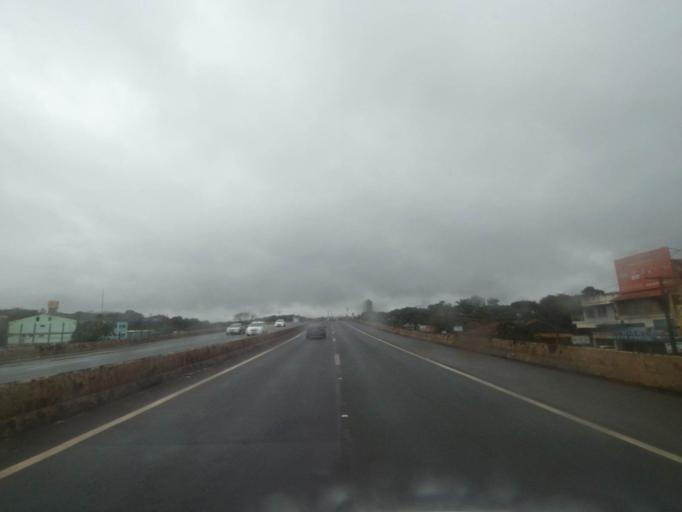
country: PY
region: Alto Parana
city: Ciudad del Este
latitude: -25.5065
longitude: -54.5871
